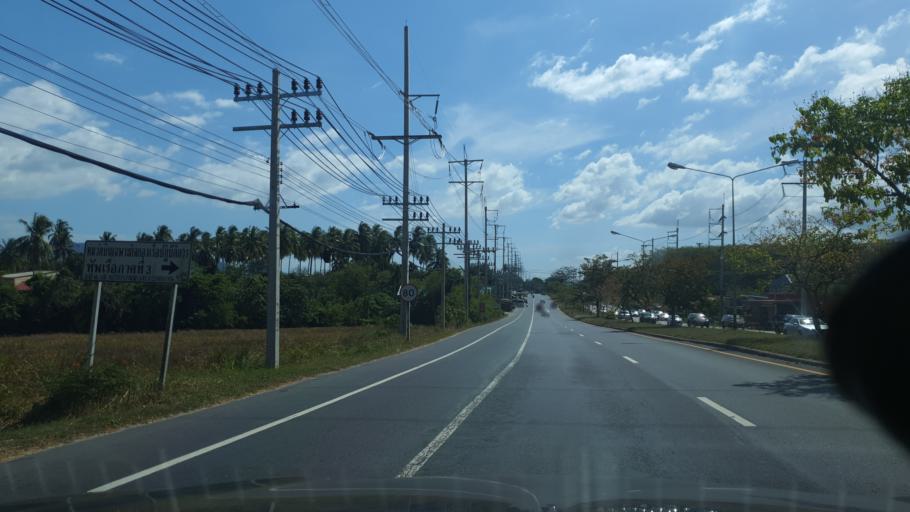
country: TH
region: Phuket
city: Thalang
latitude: 8.1227
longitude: 98.3365
